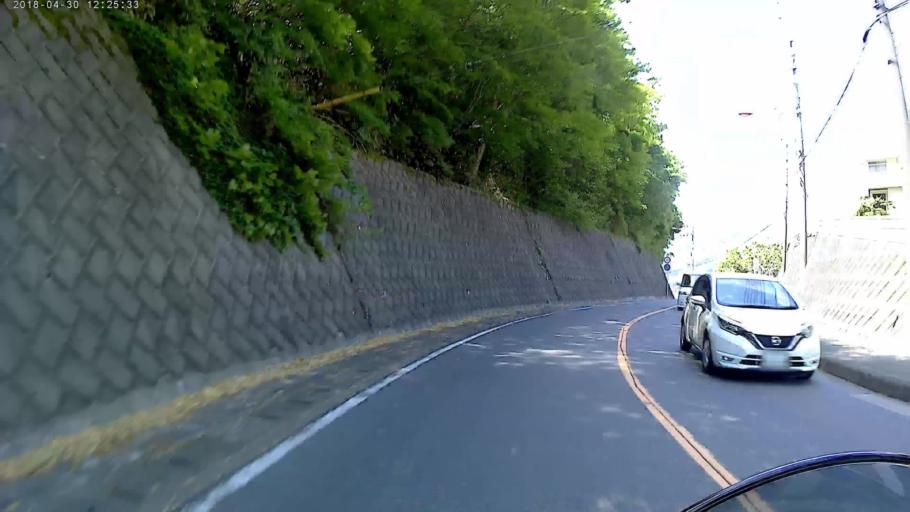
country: JP
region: Tokyo
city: Hachioji
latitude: 35.5807
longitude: 139.2727
